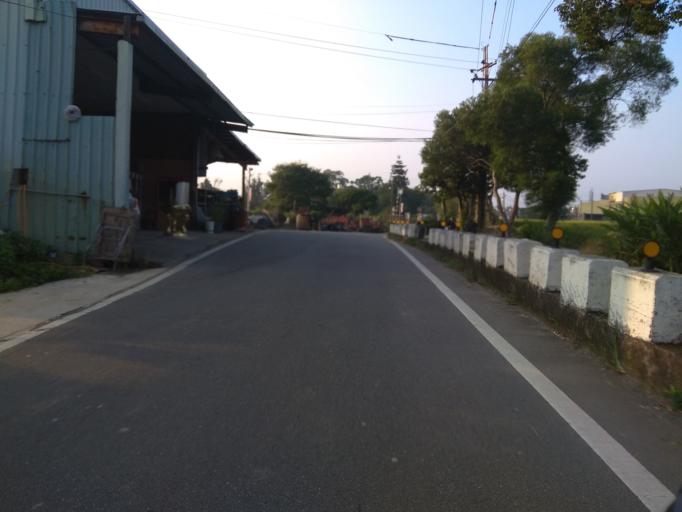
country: TW
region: Taiwan
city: Daxi
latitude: 24.9352
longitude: 121.2102
